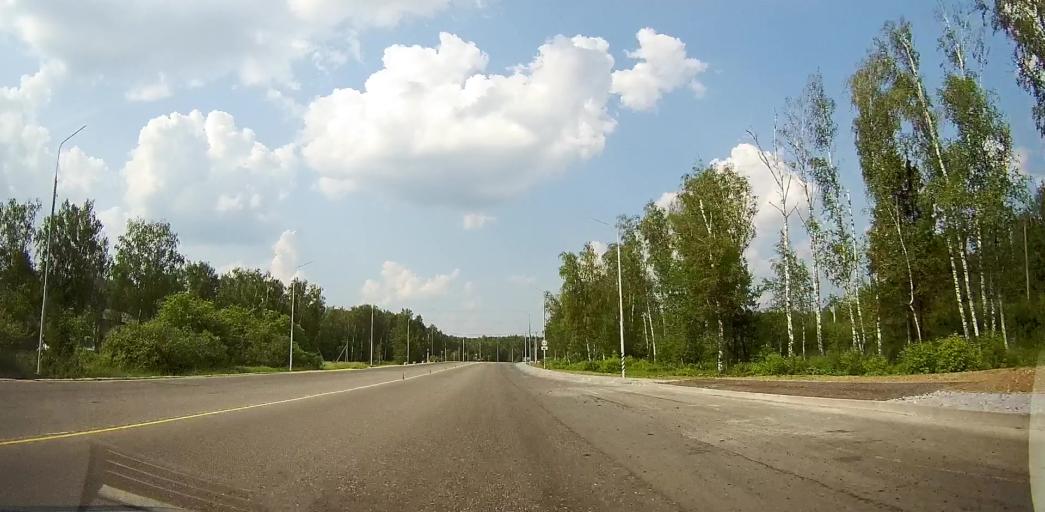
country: RU
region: Moskovskaya
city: Mikhnevo
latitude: 55.0723
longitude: 37.9519
